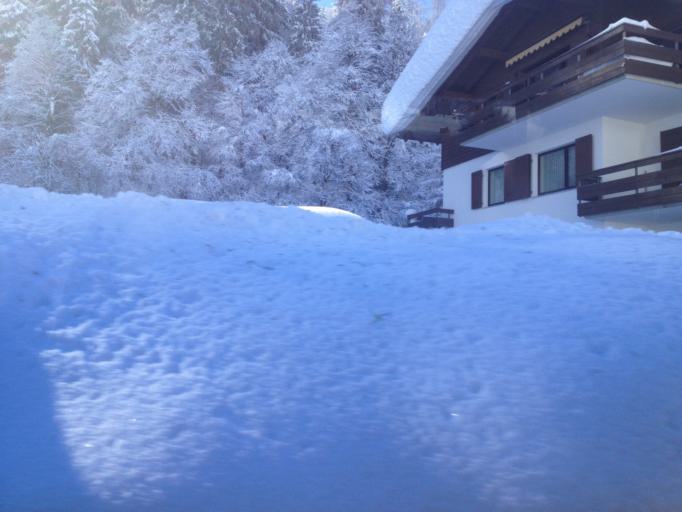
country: CH
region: Grisons
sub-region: Praettigau/Davos District
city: Klosters Serneus
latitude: 46.8618
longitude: 9.8940
